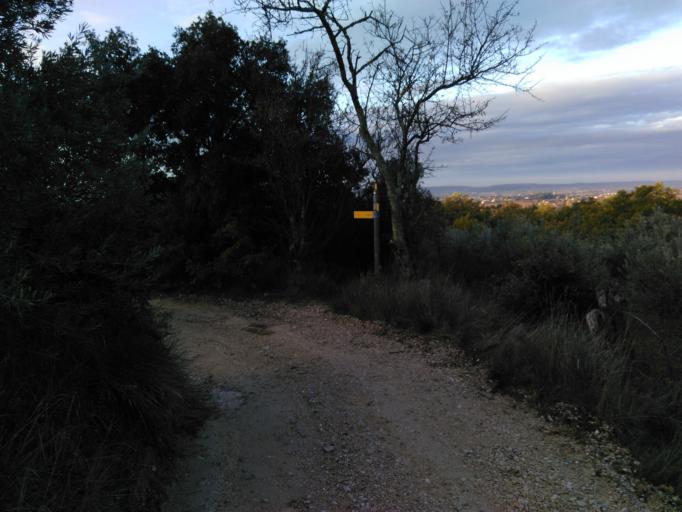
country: FR
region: Provence-Alpes-Cote d'Azur
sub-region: Departement du Vaucluse
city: Mormoiron
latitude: 44.0667
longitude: 5.1645
